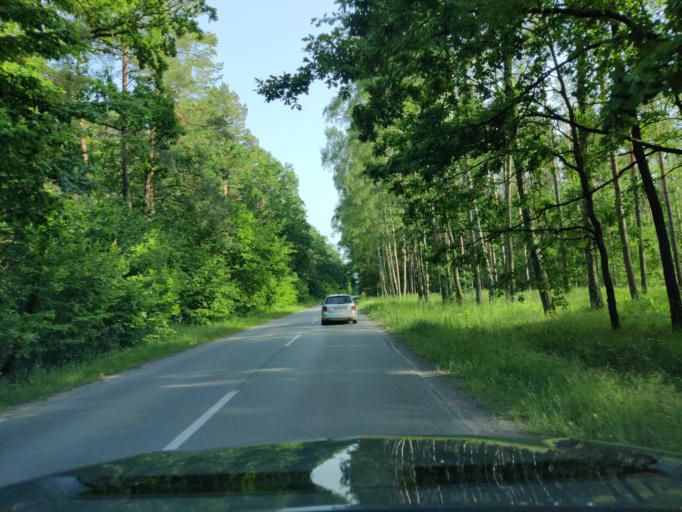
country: PL
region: Masovian Voivodeship
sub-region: Powiat wyszkowski
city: Wyszkow
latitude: 52.6305
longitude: 21.4507
